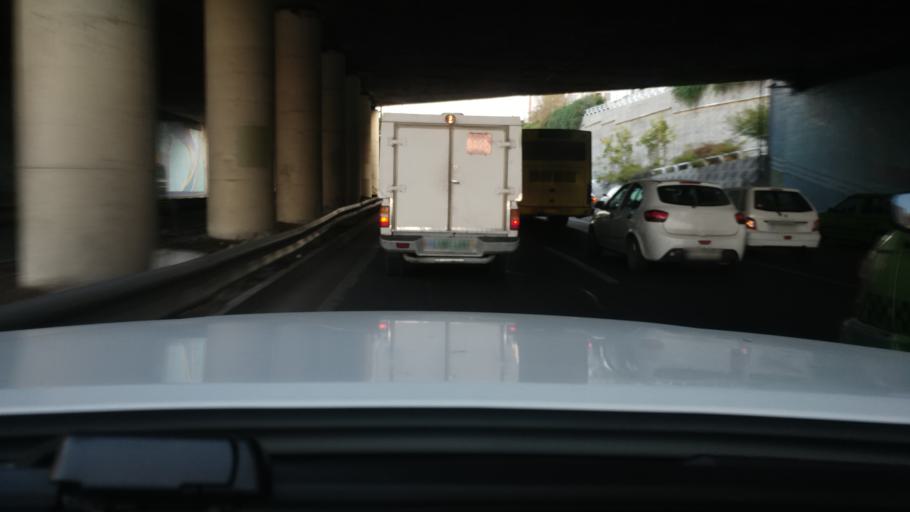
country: IR
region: Tehran
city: Tehran
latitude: 35.7318
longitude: 51.3112
